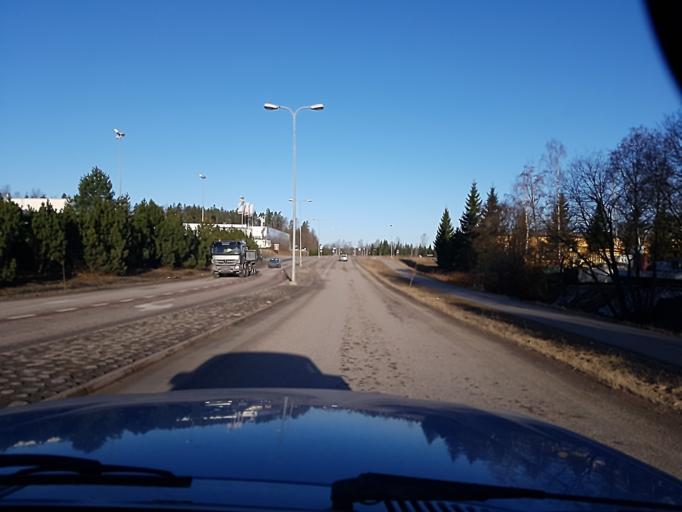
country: FI
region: Uusimaa
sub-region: Helsinki
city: Helsinki
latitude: 60.2944
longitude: 24.9096
